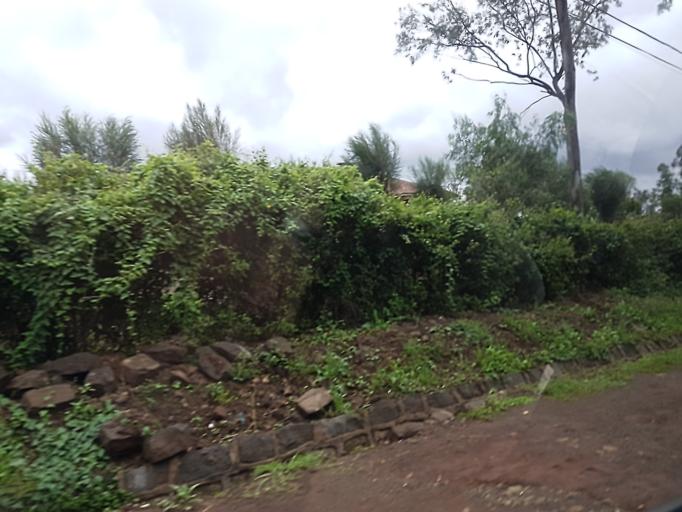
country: KE
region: Kajiado
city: Ngong
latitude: -1.3554
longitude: 36.7343
